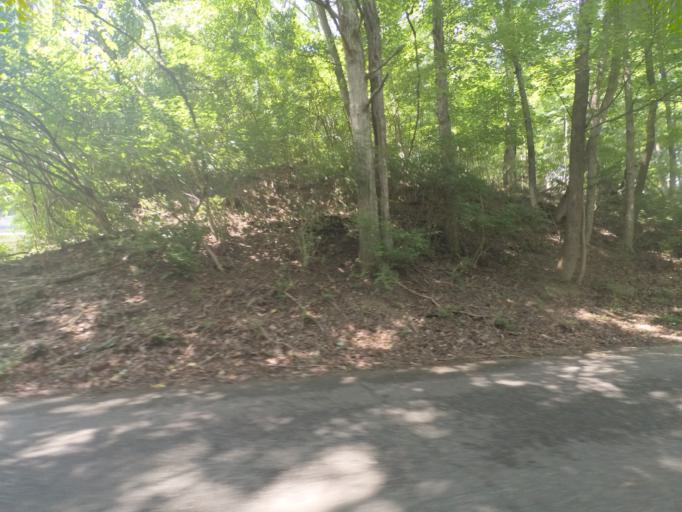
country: US
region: West Virginia
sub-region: Cabell County
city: Huntington
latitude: 38.3992
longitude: -82.4288
